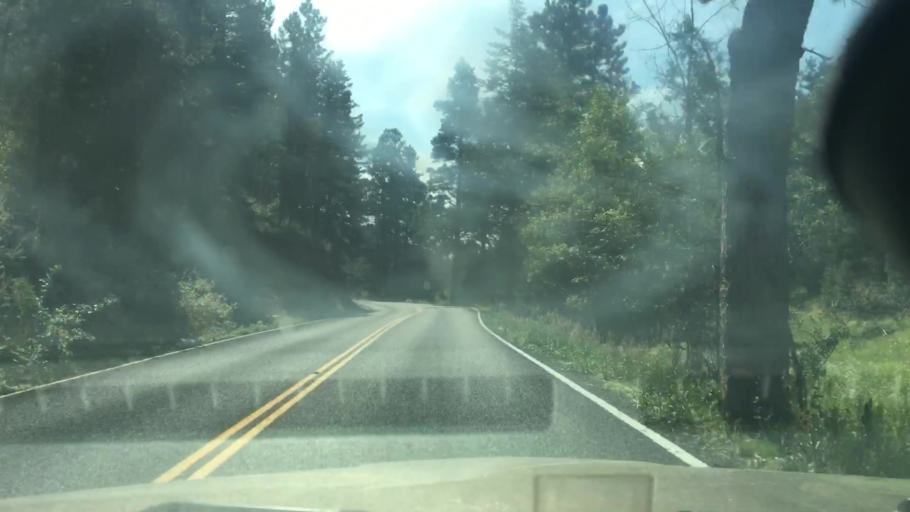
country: US
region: Colorado
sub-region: Larimer County
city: Laporte
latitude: 40.6566
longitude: -105.3747
